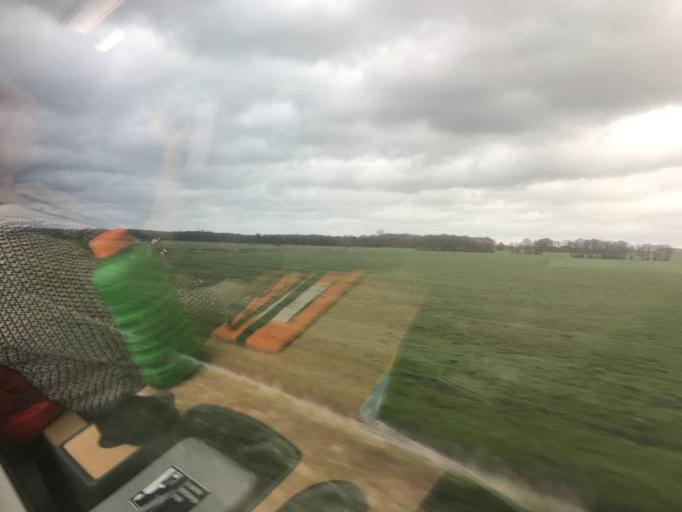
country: DE
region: Schleswig-Holstein
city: Wulfsmoor
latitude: 53.9167
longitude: 9.7347
